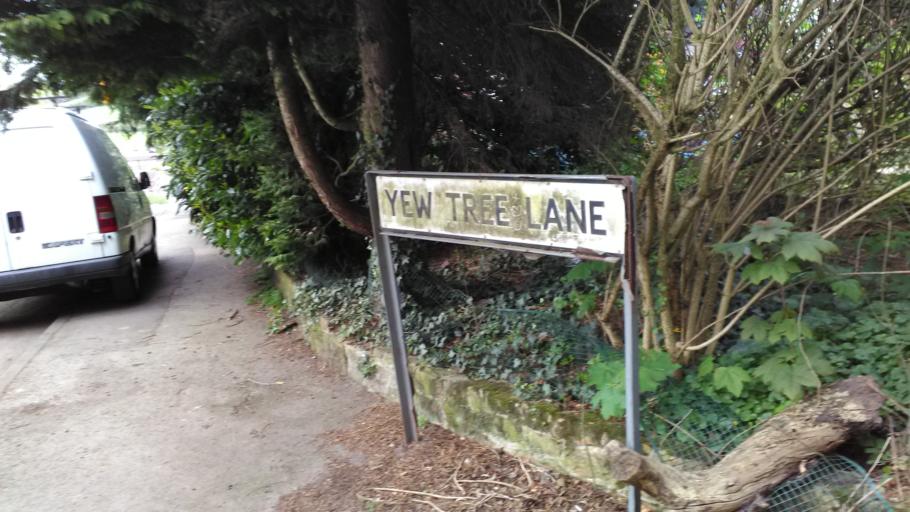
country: GB
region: England
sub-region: Nottinghamshire
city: Burton Joyce
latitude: 52.9795
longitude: -1.0696
